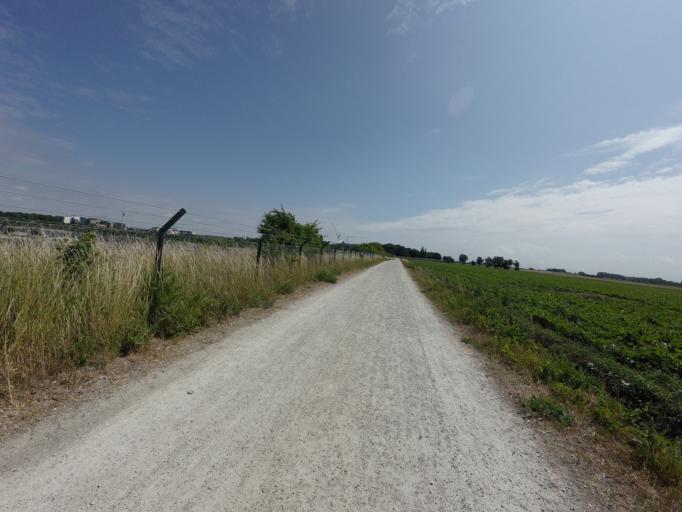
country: SE
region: Skane
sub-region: Malmo
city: Bunkeflostrand
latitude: 55.5641
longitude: 12.9360
